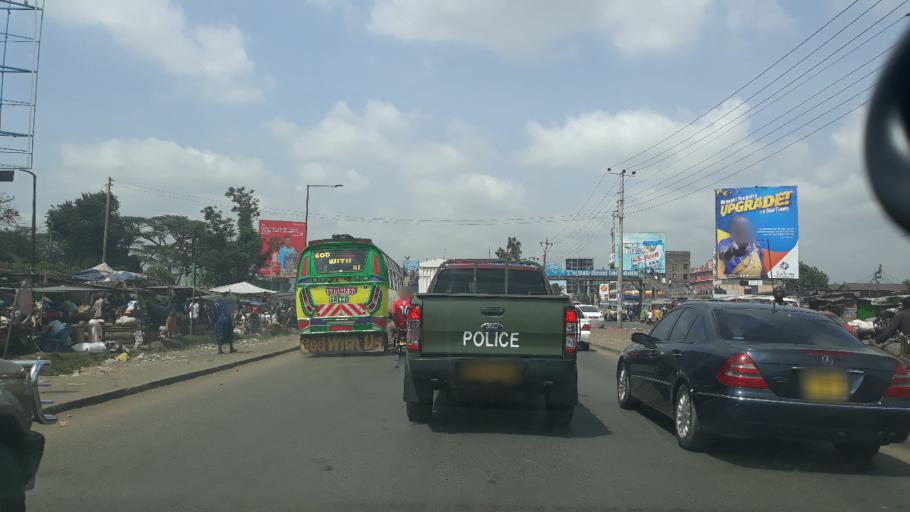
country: KE
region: Nairobi Area
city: Pumwani
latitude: -1.2928
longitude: 36.8446
